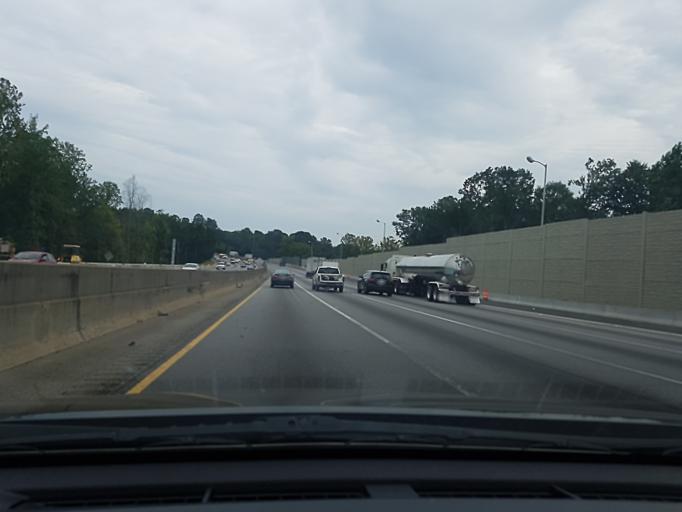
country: US
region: Georgia
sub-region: DeKalb County
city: Panthersville
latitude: 33.6989
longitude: -84.2615
